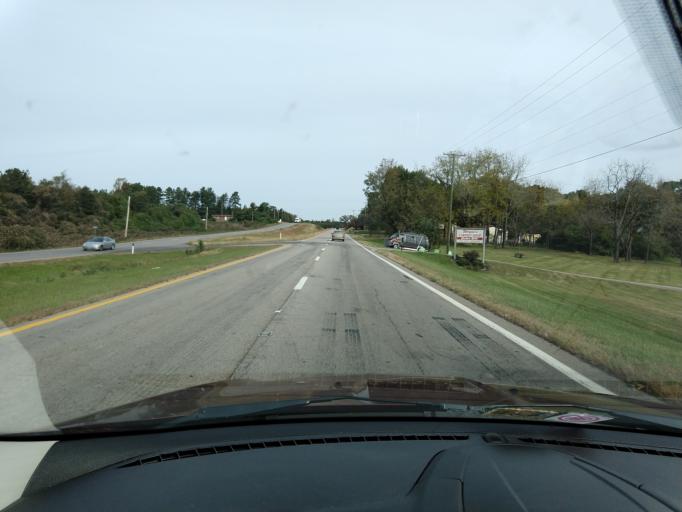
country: US
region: Virginia
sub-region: Pittsylvania County
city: Chatham
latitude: 36.8775
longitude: -79.4087
